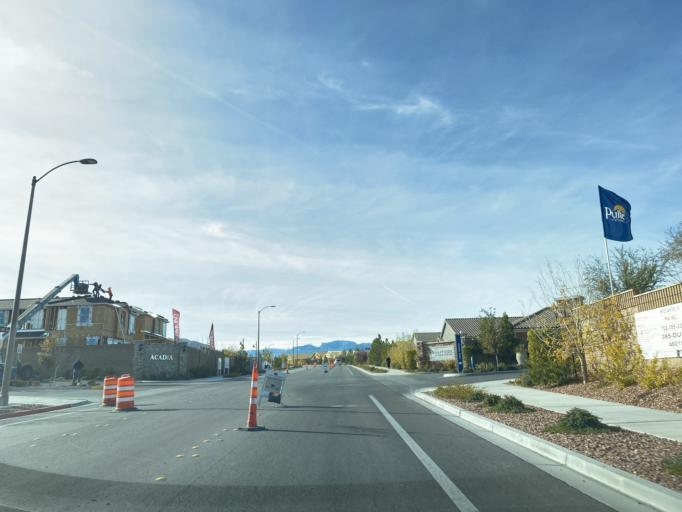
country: US
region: Nevada
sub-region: Clark County
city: Summerlin South
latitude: 36.3106
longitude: -115.3231
